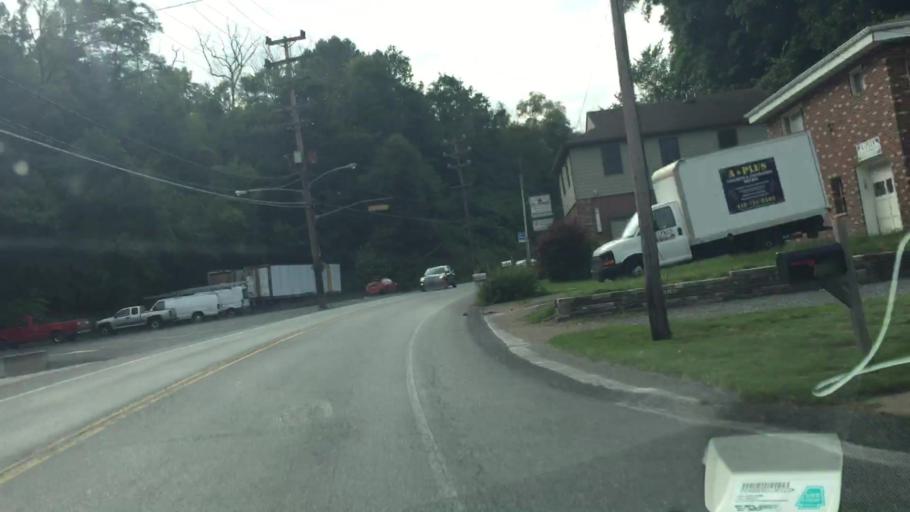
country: US
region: Pennsylvania
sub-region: Allegheny County
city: Heidelberg
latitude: 40.3745
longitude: -80.0929
